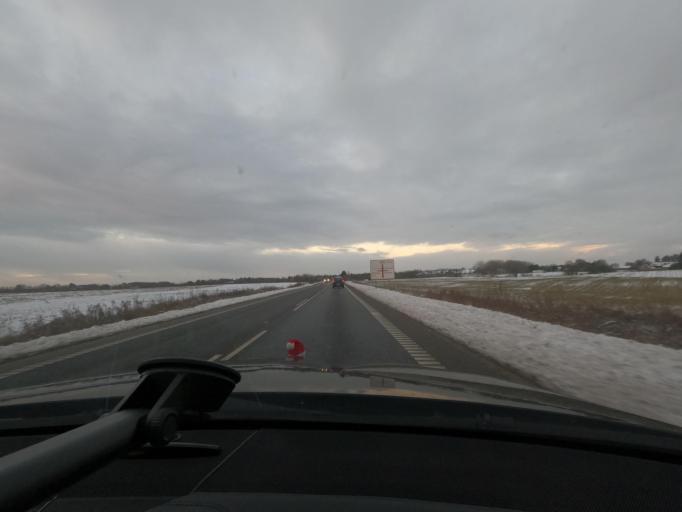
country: DK
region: South Denmark
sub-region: Aabenraa Kommune
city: Krusa
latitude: 54.8738
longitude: 9.4658
